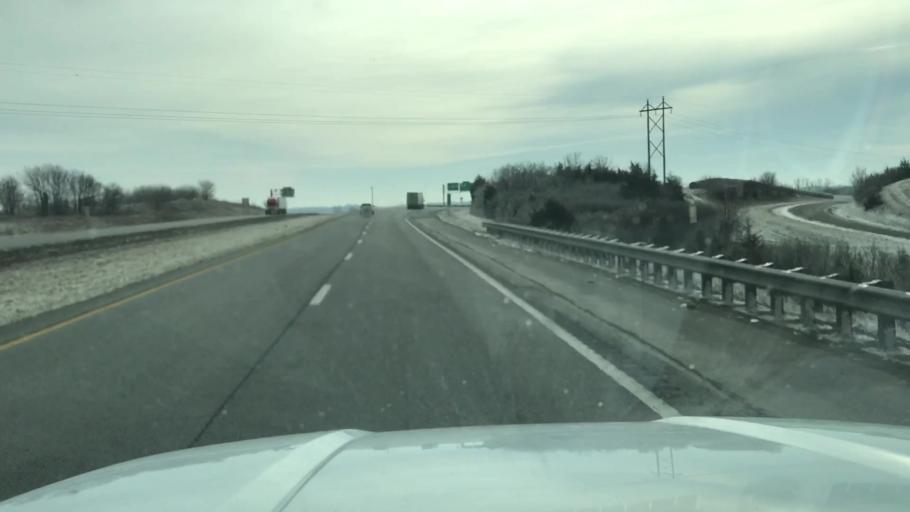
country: US
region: Missouri
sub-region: Andrew County
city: Savannah
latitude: 39.8898
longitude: -94.8623
